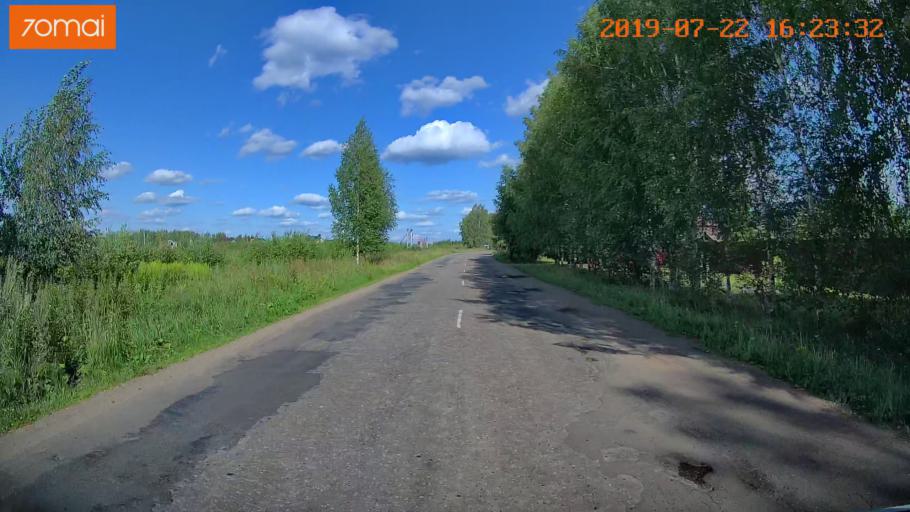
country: RU
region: Ivanovo
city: Novo-Talitsy
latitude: 57.0589
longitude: 40.8989
